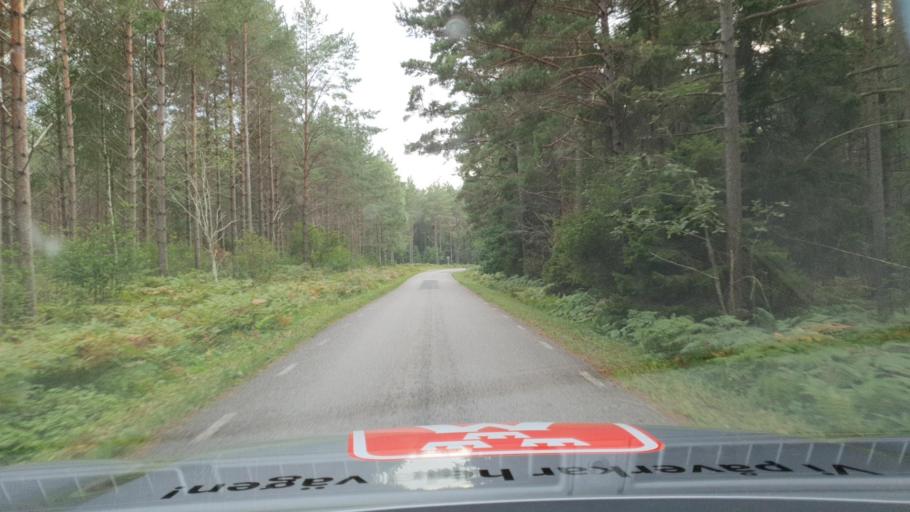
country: SE
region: Gotland
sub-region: Gotland
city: Vibble
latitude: 57.5036
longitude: 18.2607
